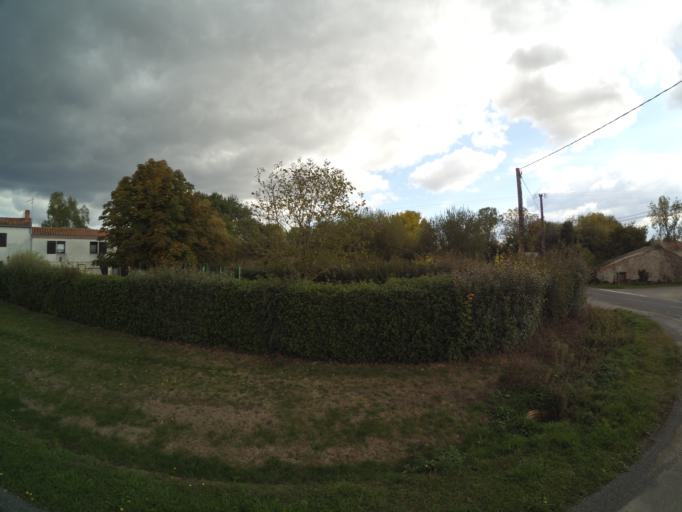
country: FR
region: Pays de la Loire
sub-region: Departement de la Loire-Atlantique
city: Remouille
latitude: 47.0583
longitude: -1.3616
